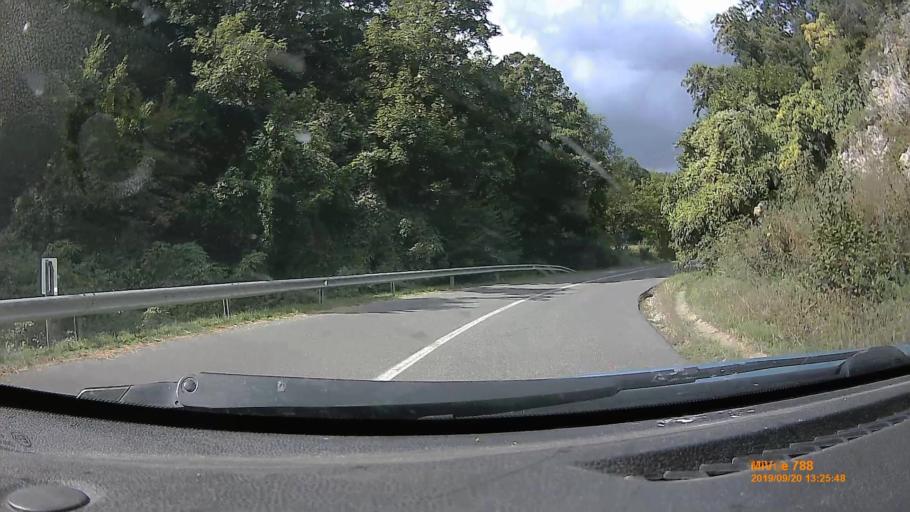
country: HU
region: Heves
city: Szilvasvarad
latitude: 48.0427
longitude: 20.4814
